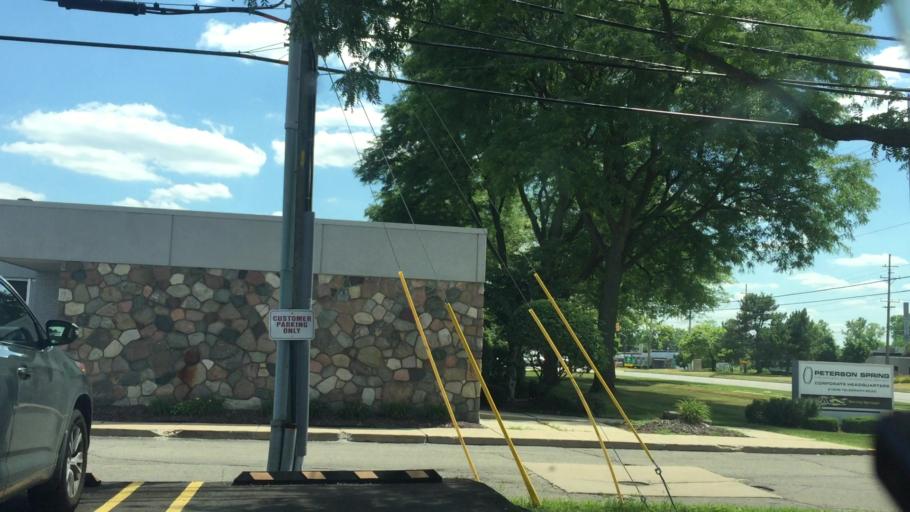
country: US
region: Michigan
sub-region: Oakland County
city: Southfield
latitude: 42.4469
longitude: -83.2775
